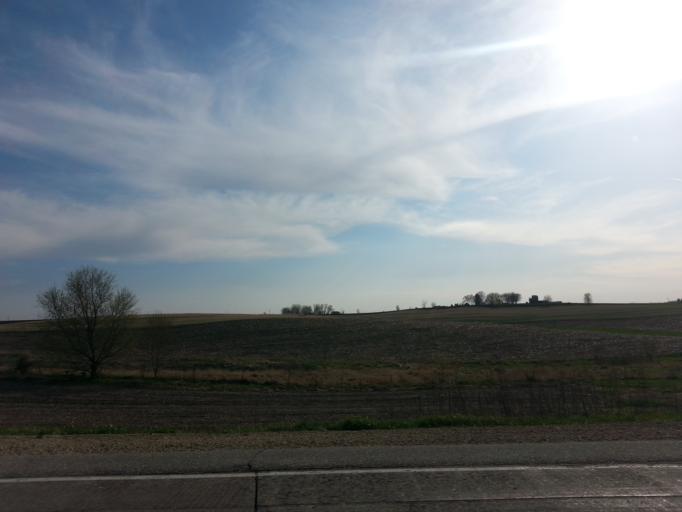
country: US
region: Wisconsin
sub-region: Pierce County
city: River Falls
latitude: 44.7383
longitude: -92.6352
